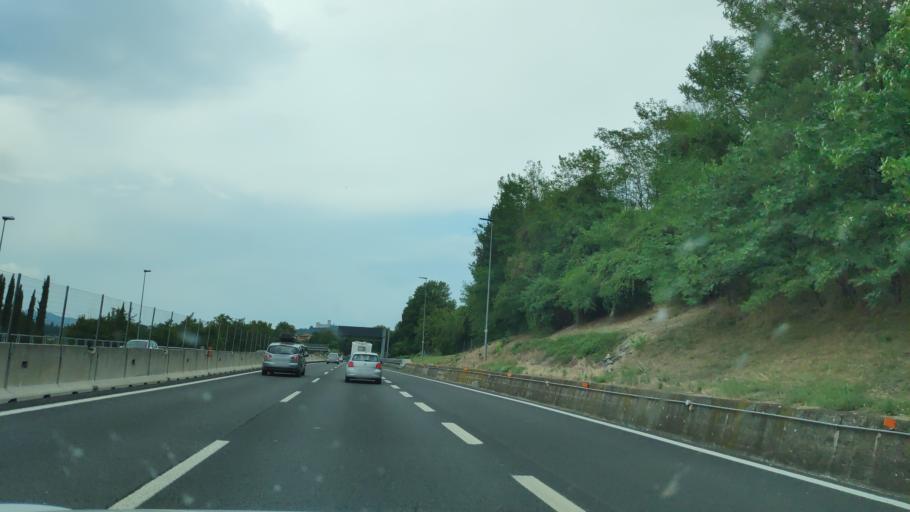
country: IT
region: Tuscany
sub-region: Province of Florence
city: Incisa in Val d'Arno
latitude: 43.6535
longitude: 11.4656
